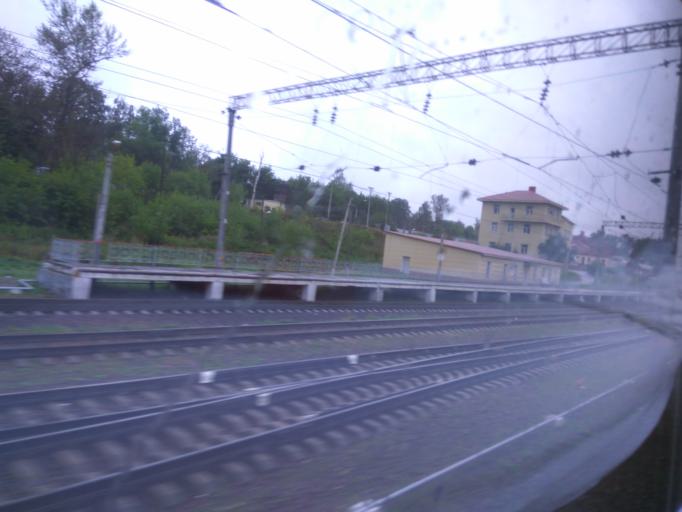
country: RU
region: Moskovskaya
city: Kashira
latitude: 54.8579
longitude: 38.1922
